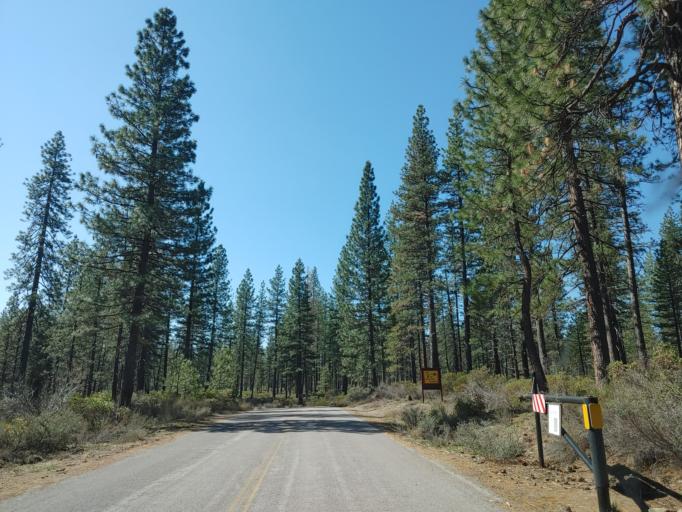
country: US
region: California
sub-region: Siskiyou County
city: McCloud
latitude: 41.2557
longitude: -122.0302
